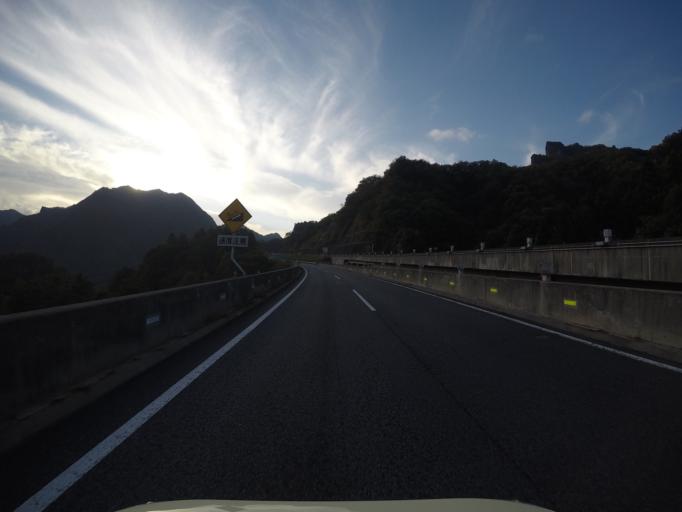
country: JP
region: Nagano
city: Saku
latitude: 36.3124
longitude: 138.6782
